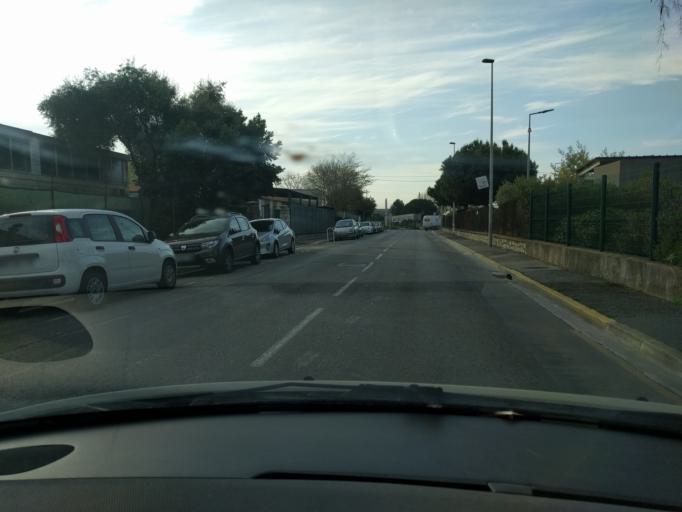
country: FR
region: Provence-Alpes-Cote d'Azur
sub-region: Departement des Alpes-Maritimes
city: Mandelieu-la-Napoule
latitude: 43.5470
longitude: 6.9665
